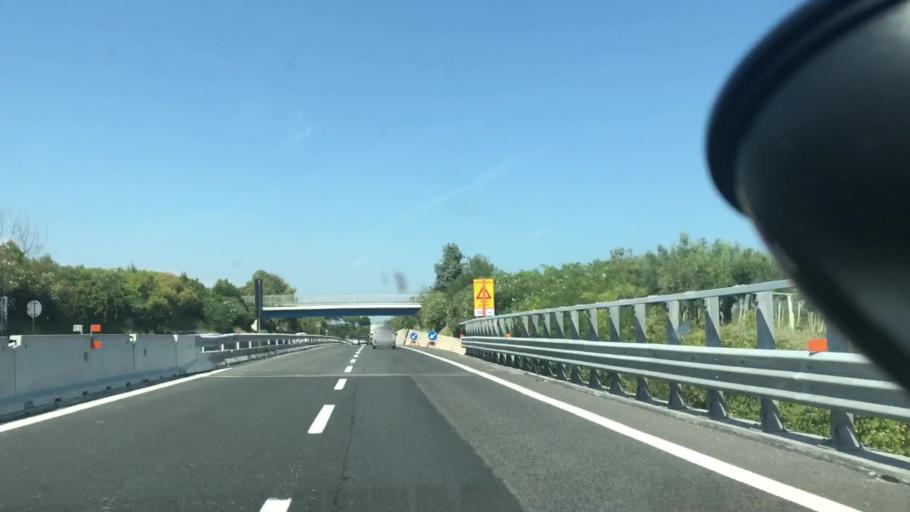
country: IT
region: Abruzzo
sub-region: Provincia di Chieti
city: Tollo
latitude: 42.3659
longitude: 14.3222
